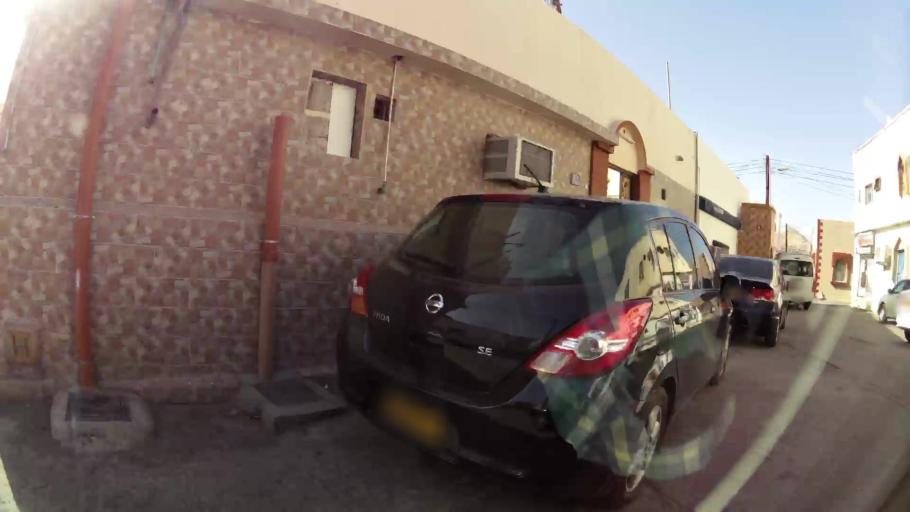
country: OM
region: Muhafazat Masqat
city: Muscat
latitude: 23.5833
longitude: 58.5197
